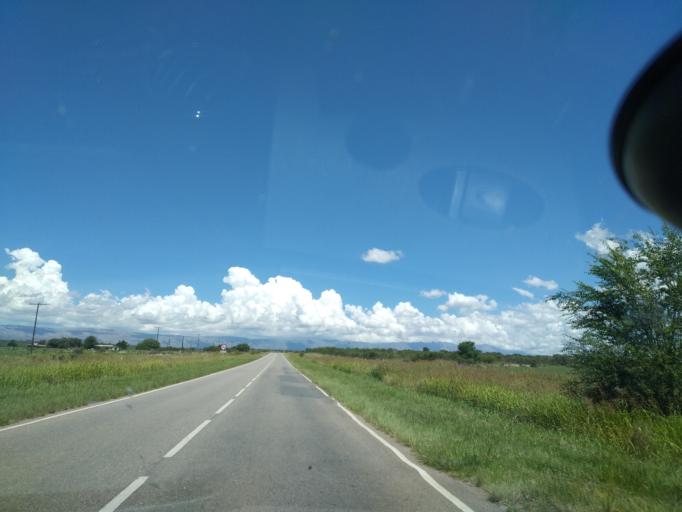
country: AR
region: Cordoba
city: Villa Cura Brochero
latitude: -31.6747
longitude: -65.0898
